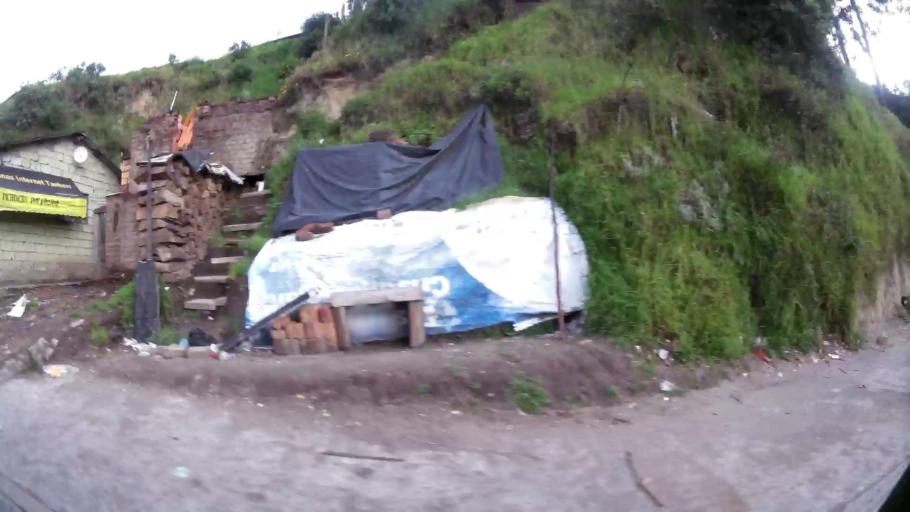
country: EC
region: Pichincha
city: Quito
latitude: -0.2950
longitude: -78.5272
